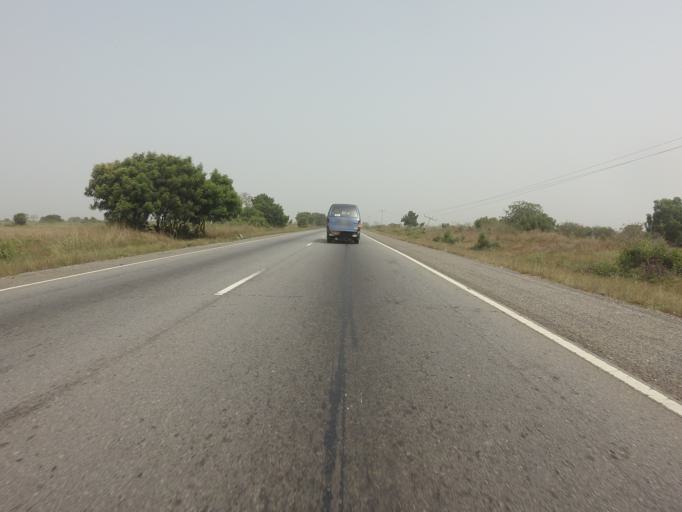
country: GH
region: Volta
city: Anloga
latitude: 5.8859
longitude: 0.4434
